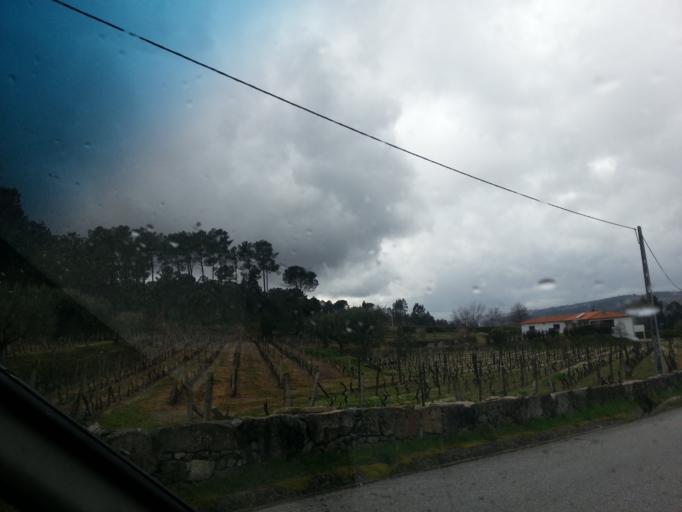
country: PT
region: Viseu
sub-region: Viseu
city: Rio de Loba
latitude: 40.6061
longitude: -7.8519
